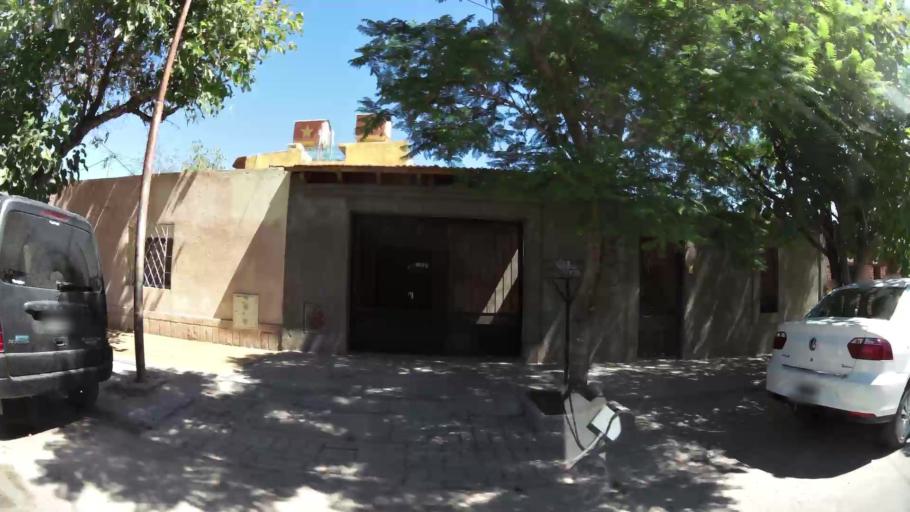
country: AR
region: San Juan
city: San Juan
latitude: -31.5179
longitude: -68.5206
